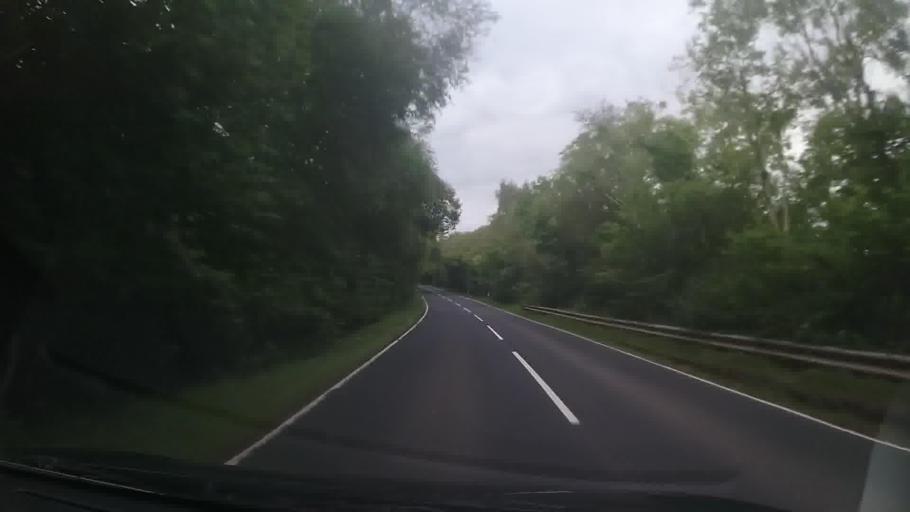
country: GB
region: Scotland
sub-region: Argyll and Bute
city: Garelochhead
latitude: 56.2089
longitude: -5.0576
